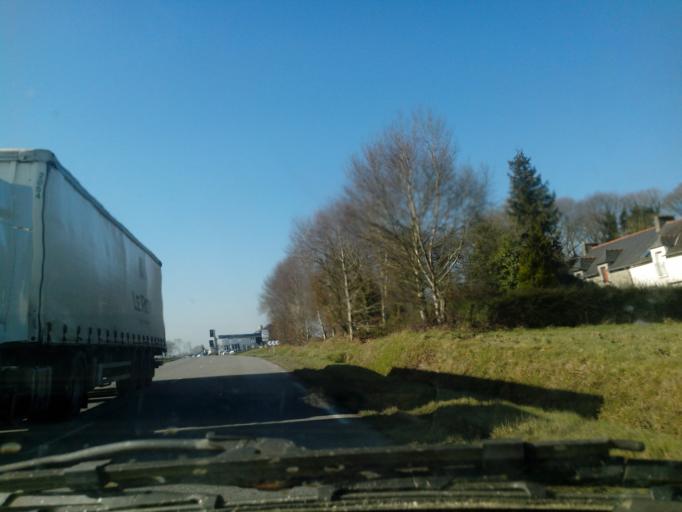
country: FR
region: Brittany
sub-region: Departement du Morbihan
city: Meneac
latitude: 48.1987
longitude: -2.4784
